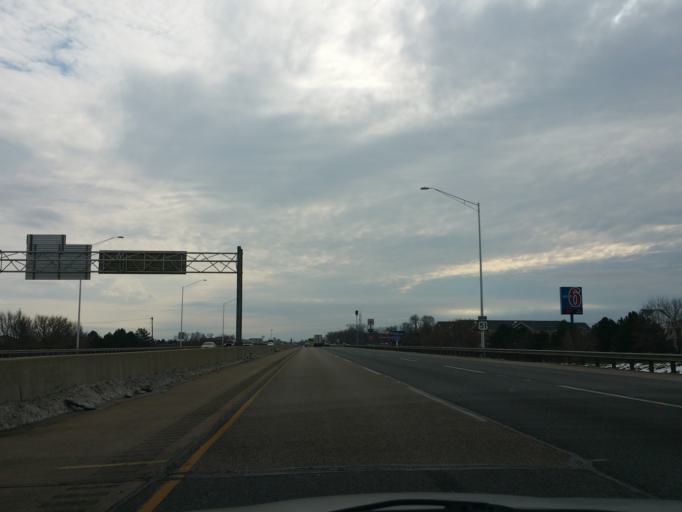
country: US
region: Illinois
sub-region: Winnebago County
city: Cherry Valley
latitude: 42.2739
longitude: -88.9649
